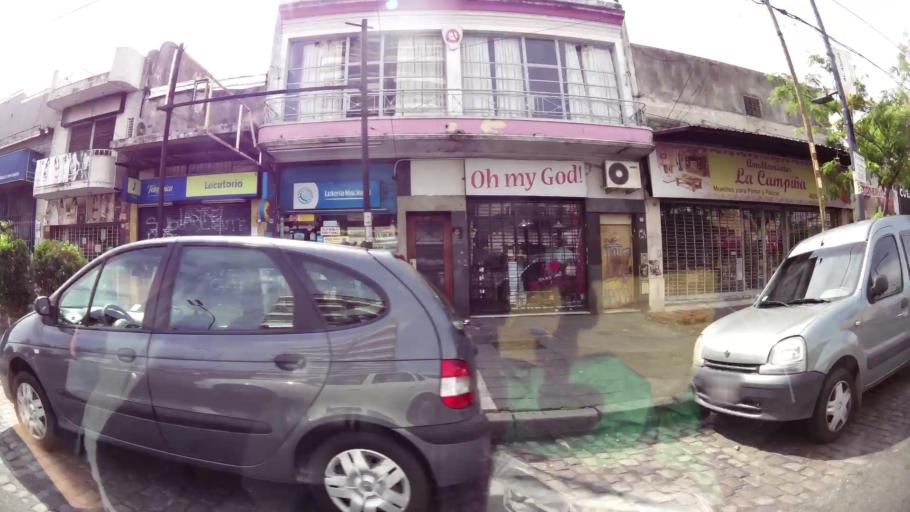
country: AR
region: Buenos Aires F.D.
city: Villa Lugano
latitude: -34.6502
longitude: -58.5010
